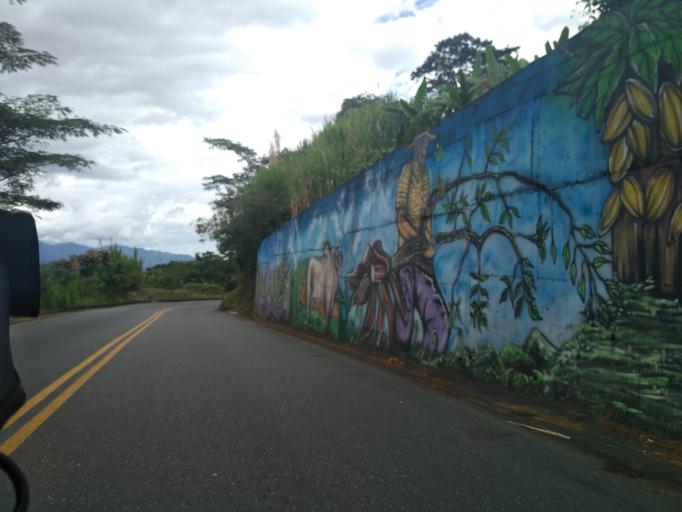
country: CO
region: Cauca
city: Rosas
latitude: 2.2498
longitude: -76.7658
